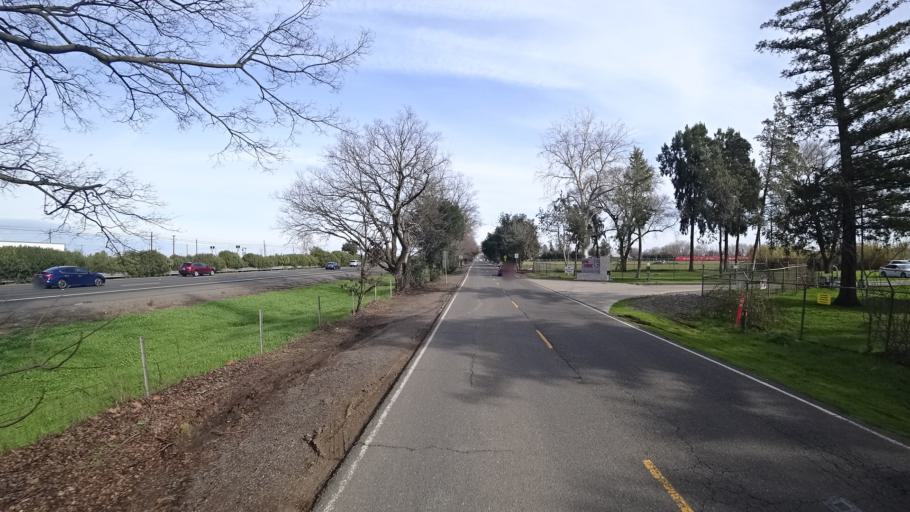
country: US
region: California
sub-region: Yolo County
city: Davis
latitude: 38.5566
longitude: -121.6765
